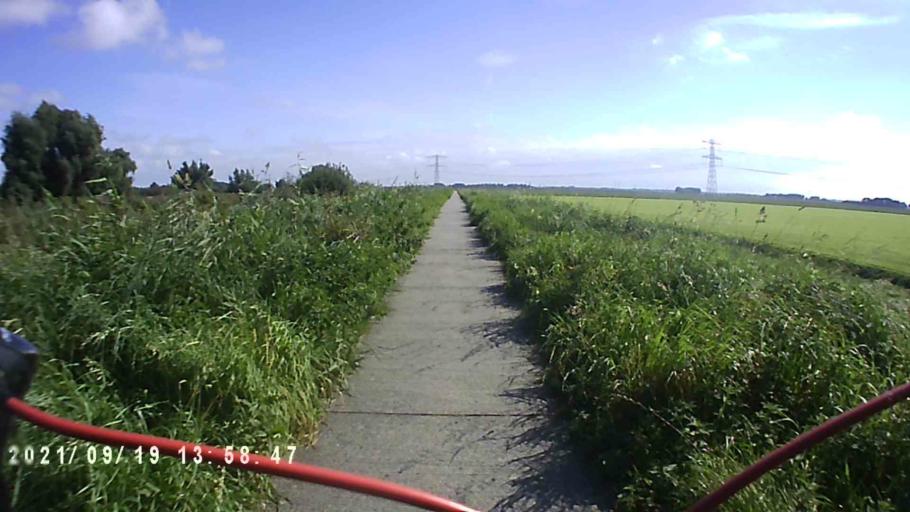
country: NL
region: Groningen
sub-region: Gemeente  Oldambt
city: Winschoten
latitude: 53.1431
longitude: 7.0955
